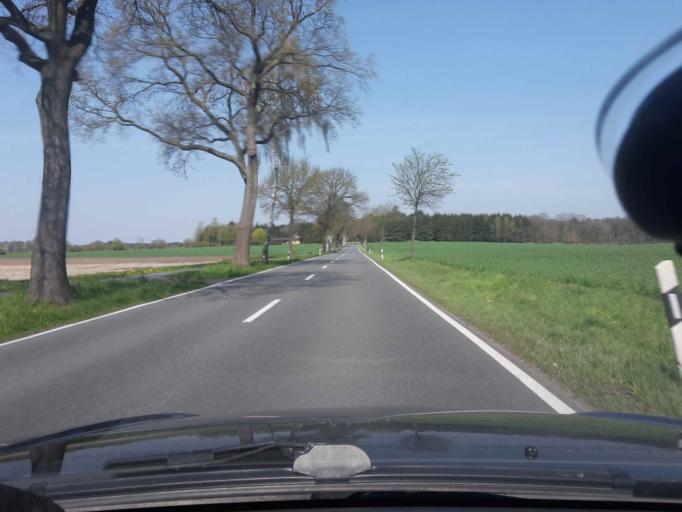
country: DE
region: Lower Saxony
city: Schneverdingen
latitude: 53.0842
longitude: 9.8526
